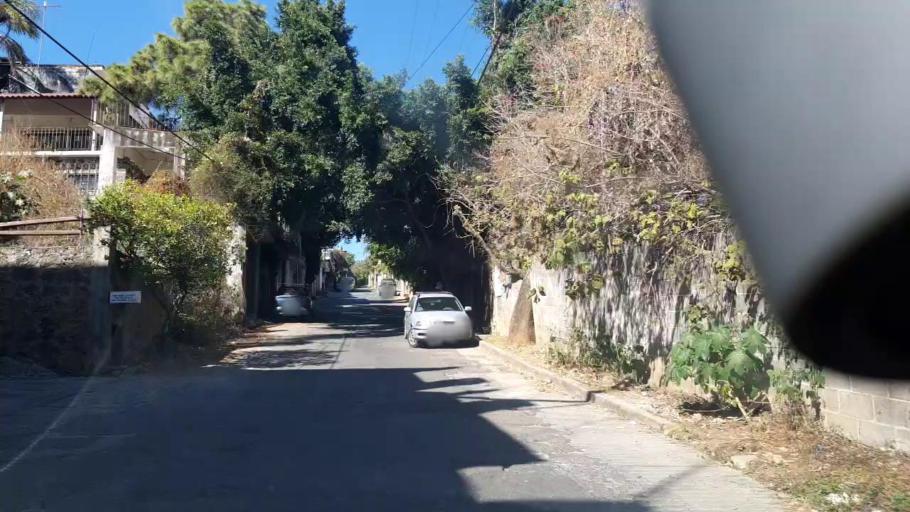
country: MX
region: Morelos
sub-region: Cuernavaca
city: Lomas de Ahuatepec
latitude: 18.9726
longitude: -99.2136
